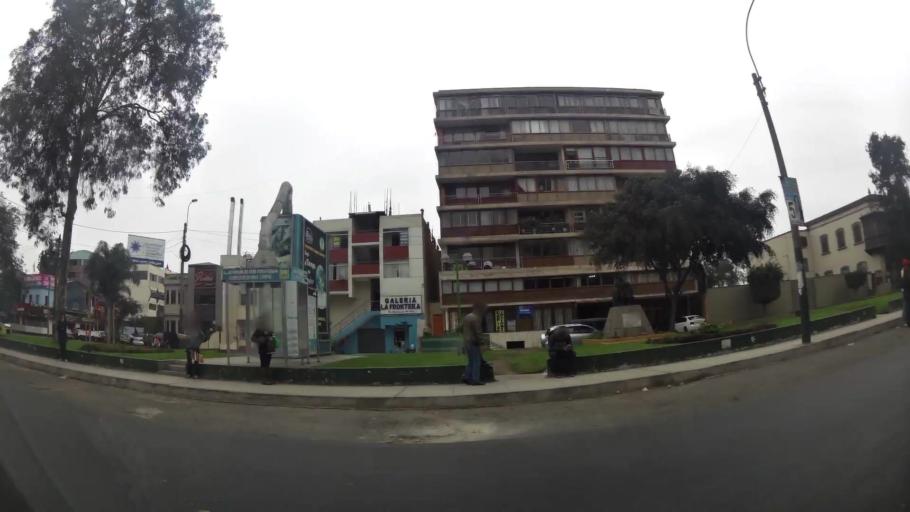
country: PE
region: Lima
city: Lima
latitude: -12.0719
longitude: -77.0411
